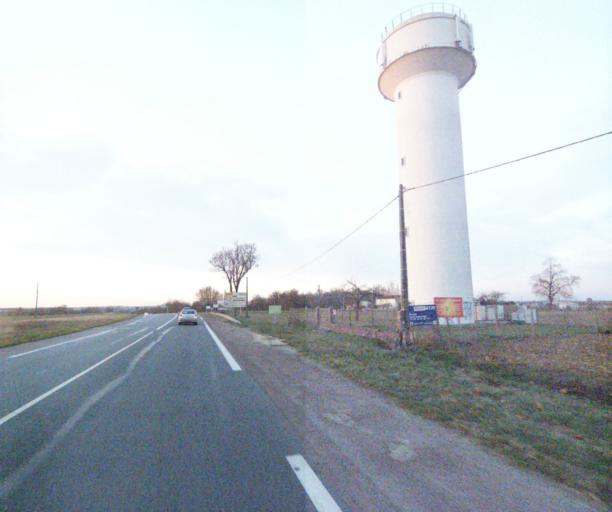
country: FR
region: Poitou-Charentes
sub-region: Departement de la Charente-Maritime
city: Saint-Porchaire
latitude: 45.8096
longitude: -0.7620
